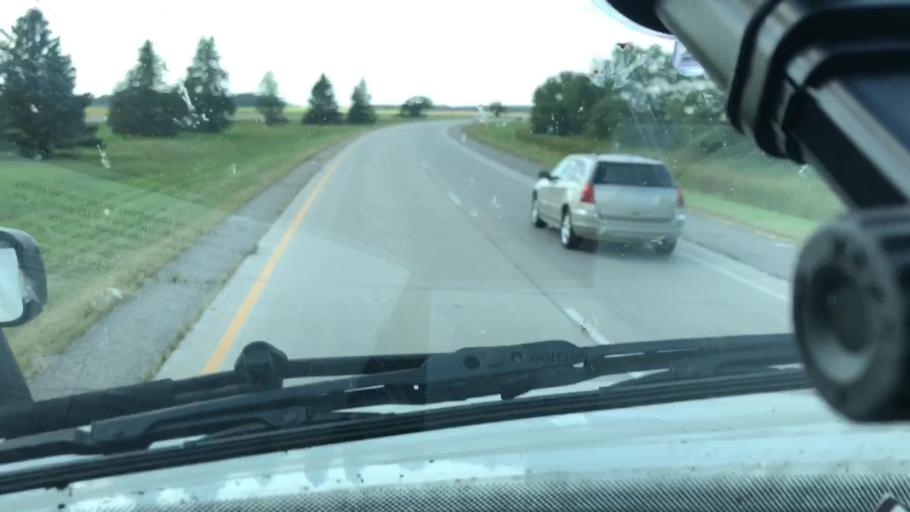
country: US
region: Minnesota
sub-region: Mower County
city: Austin
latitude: 43.6620
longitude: -93.0307
